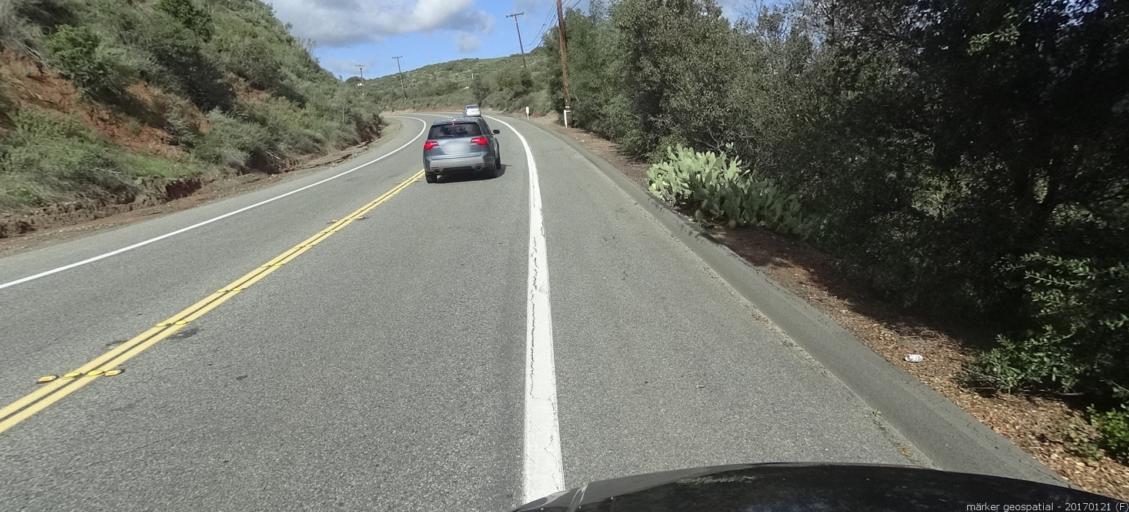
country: US
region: California
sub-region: Orange County
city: Foothill Ranch
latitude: 33.7510
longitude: -117.6810
